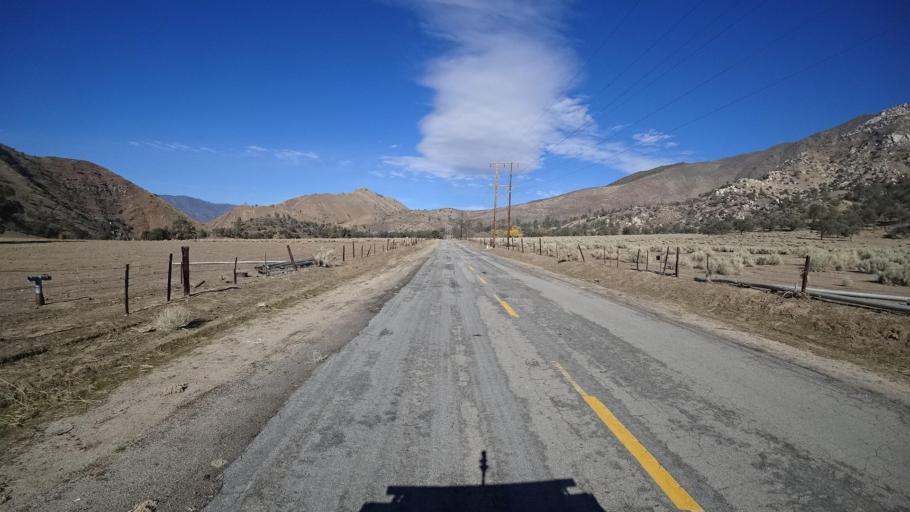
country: US
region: California
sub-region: Kern County
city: Bodfish
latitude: 35.5393
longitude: -118.5103
